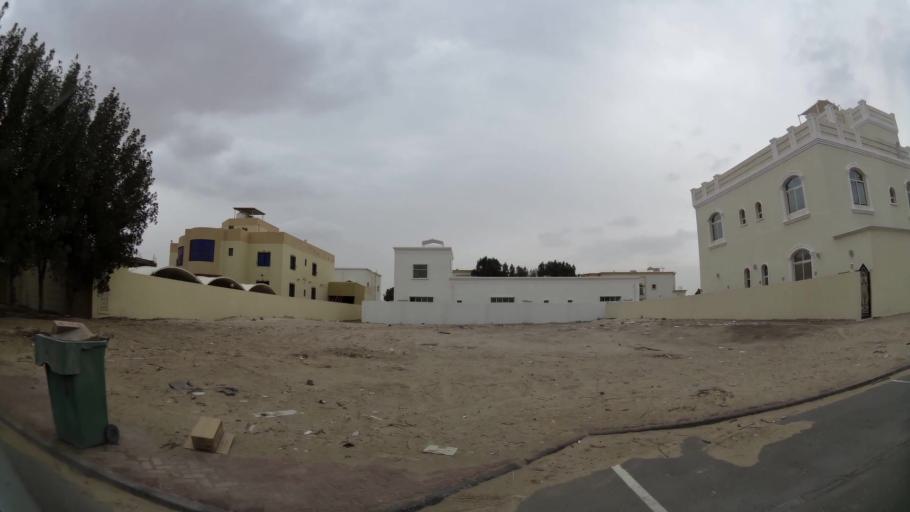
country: AE
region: Abu Dhabi
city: Abu Dhabi
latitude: 24.3764
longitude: 54.6501
